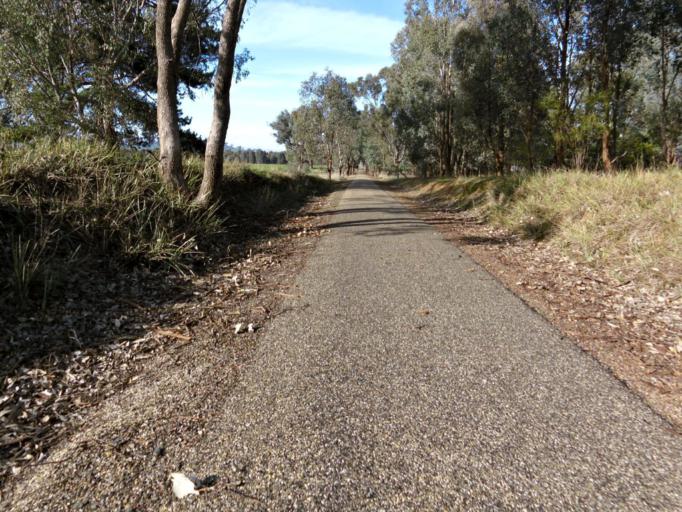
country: AU
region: Victoria
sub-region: Wangaratta
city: Wangaratta
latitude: -36.4163
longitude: 146.5500
